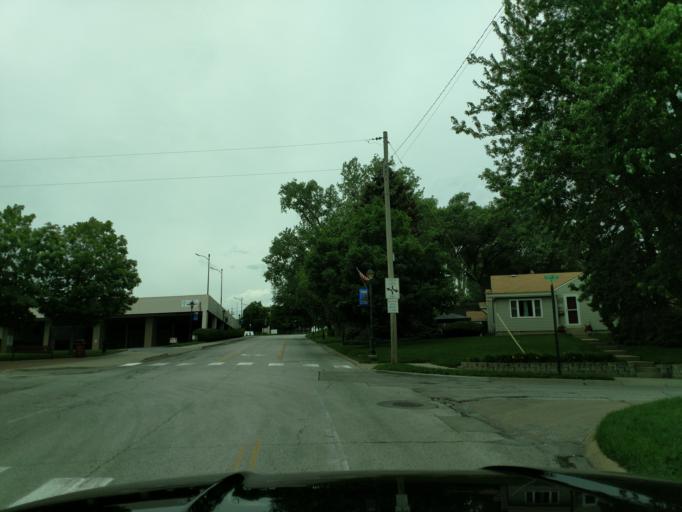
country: US
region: Nebraska
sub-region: Douglas County
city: Ralston
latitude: 41.2020
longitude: -96.0275
